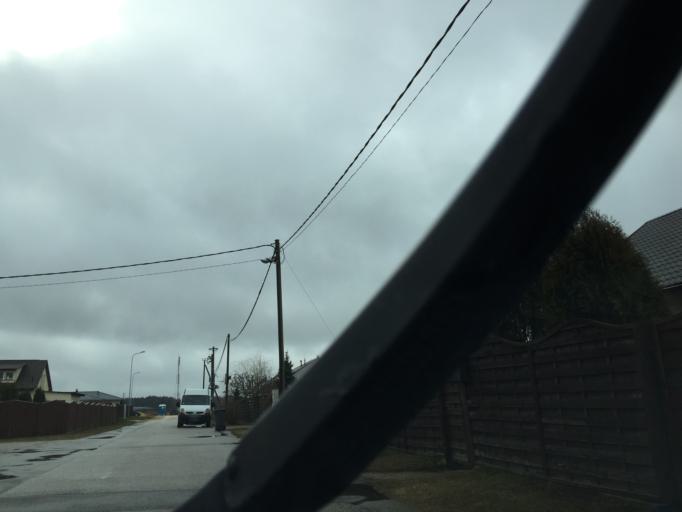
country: LV
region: Adazi
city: Adazi
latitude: 57.0689
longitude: 24.3429
